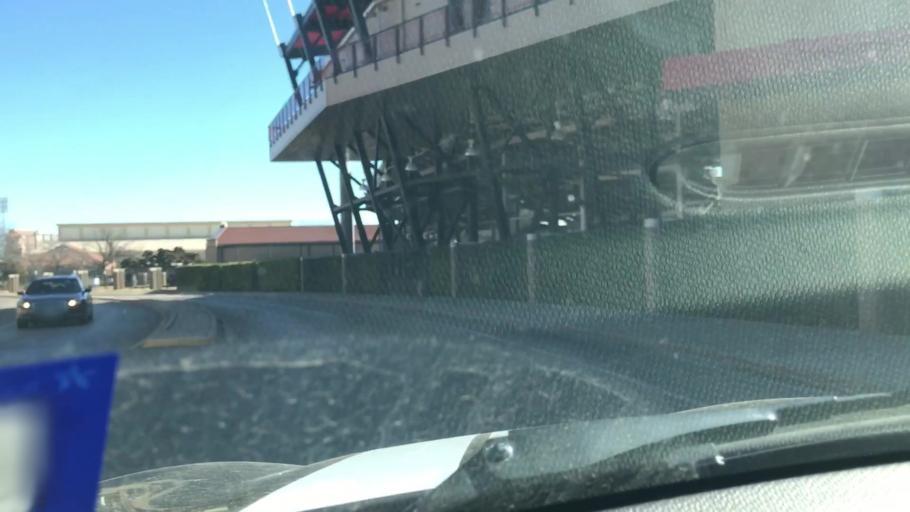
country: US
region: Texas
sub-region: Lubbock County
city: Lubbock
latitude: 33.5894
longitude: -101.8776
